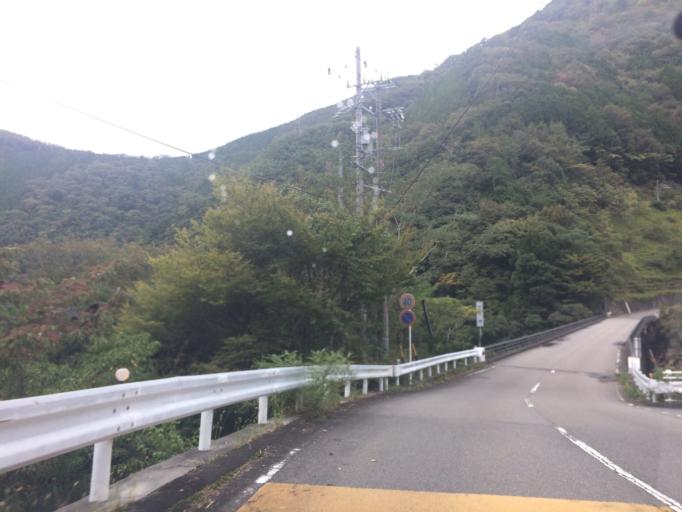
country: JP
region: Shizuoka
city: Shizuoka-shi
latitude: 35.1662
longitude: 138.1509
